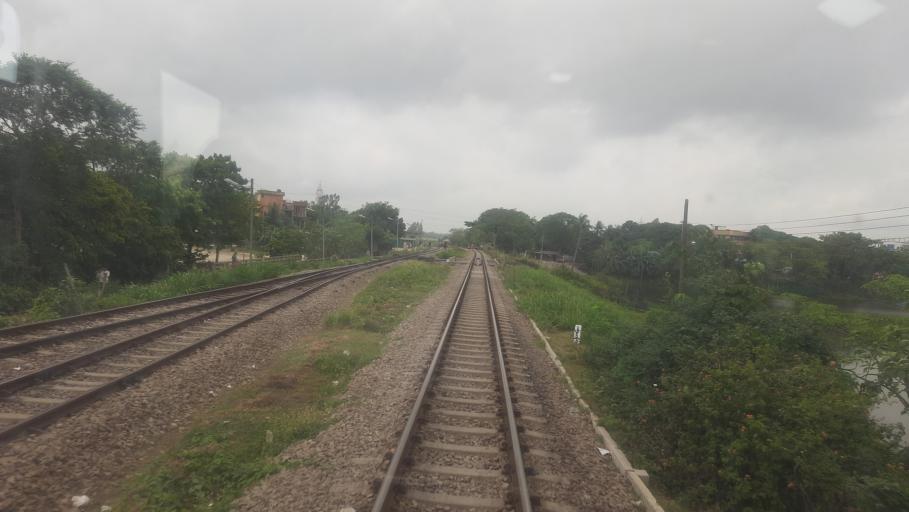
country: BD
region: Dhaka
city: Bhairab Bazar
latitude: 24.0503
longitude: 90.9739
